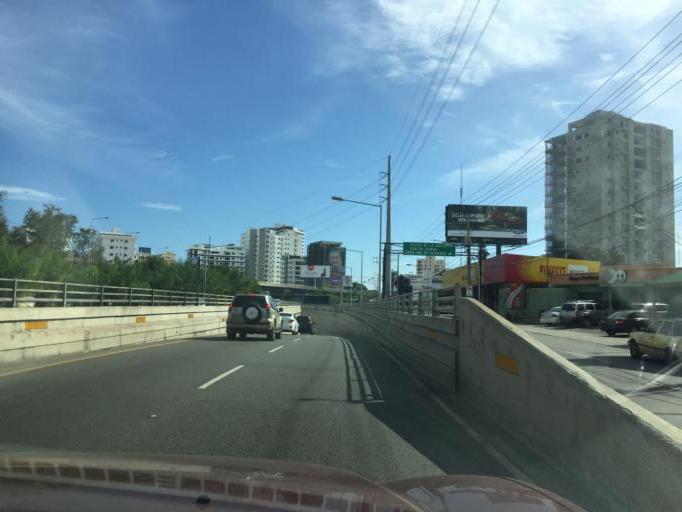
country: DO
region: Nacional
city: La Julia
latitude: 18.4747
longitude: -69.9203
